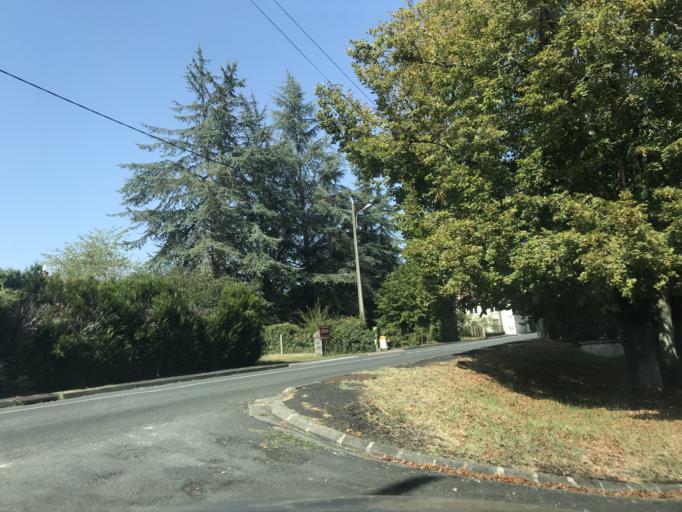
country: FR
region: Aquitaine
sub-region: Departement de la Dordogne
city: Neuvic
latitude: 45.1366
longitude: 0.4496
